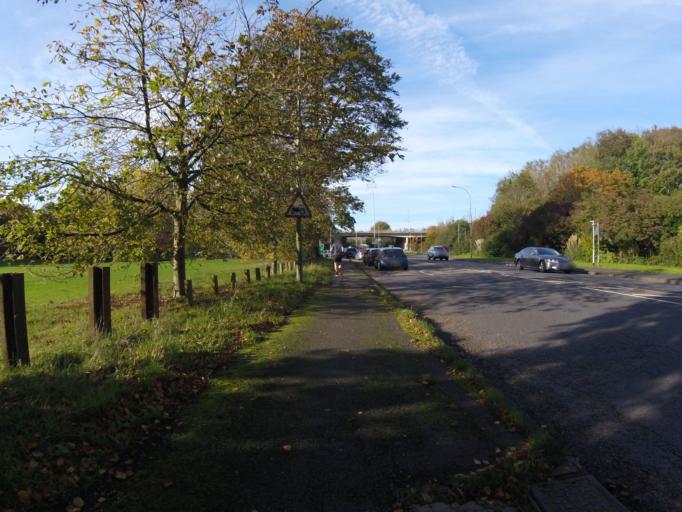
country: GB
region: England
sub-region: Brighton and Hove
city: Hove
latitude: 50.8670
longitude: -0.1550
